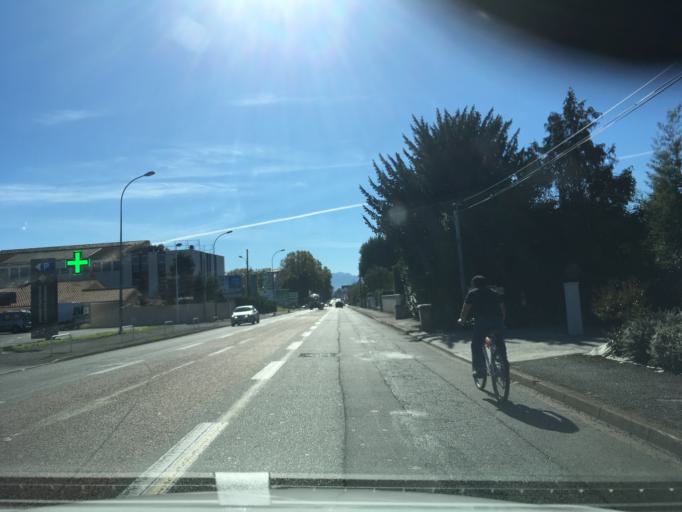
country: FR
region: Aquitaine
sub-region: Departement des Pyrenees-Atlantiques
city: Lons
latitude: 43.3324
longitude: -0.3798
